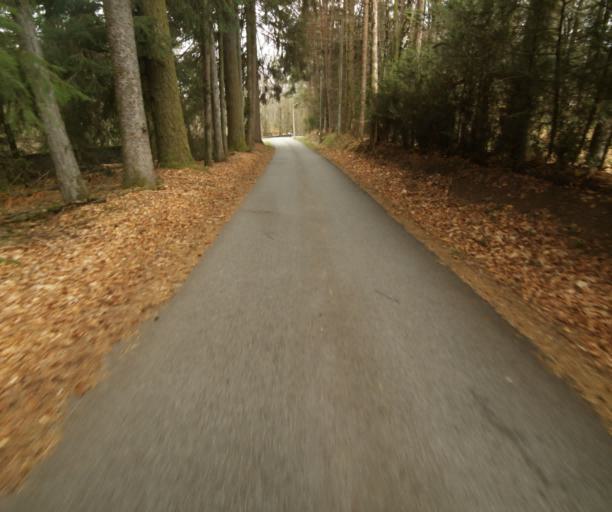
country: FR
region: Limousin
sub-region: Departement de la Correze
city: Correze
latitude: 45.3367
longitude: 1.9505
